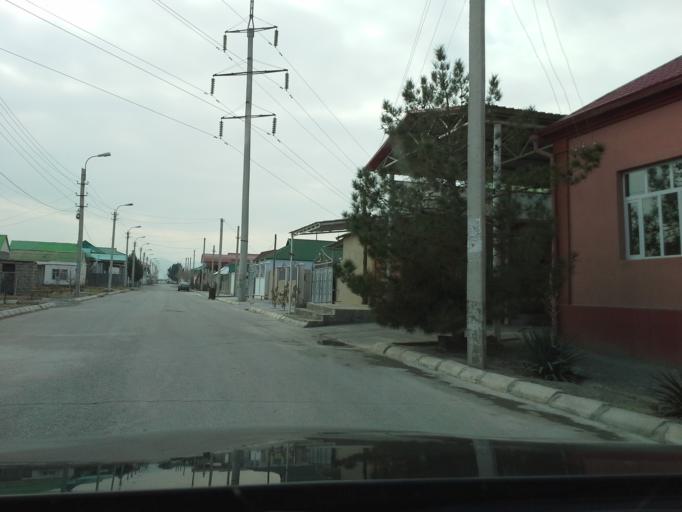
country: TM
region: Ahal
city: Abadan
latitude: 38.0426
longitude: 58.2717
